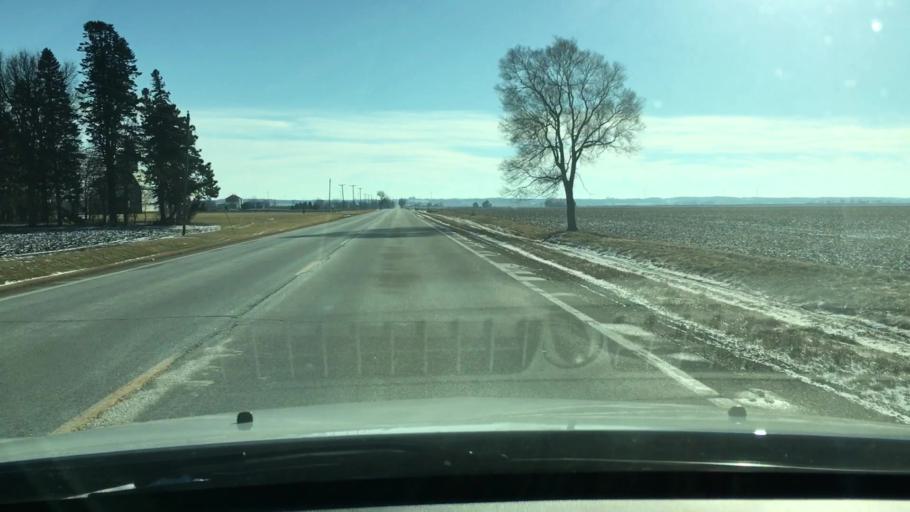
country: US
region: Illinois
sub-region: Ogle County
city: Rochelle
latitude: 41.7833
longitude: -89.0836
